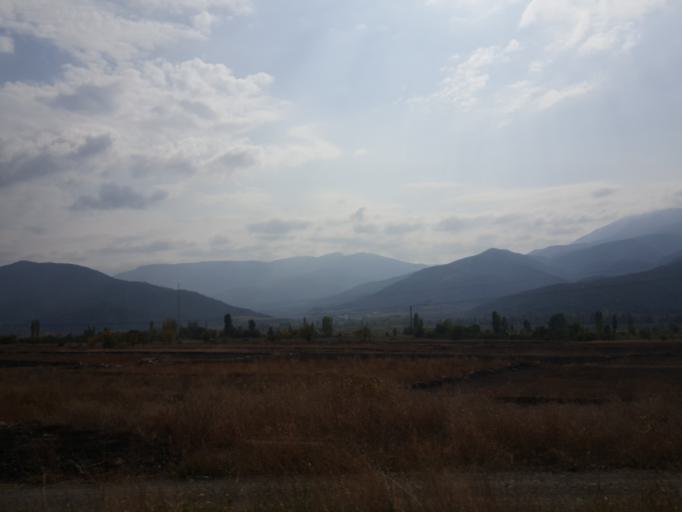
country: TR
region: Corum
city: Hacihamza
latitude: 41.1185
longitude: 34.4061
